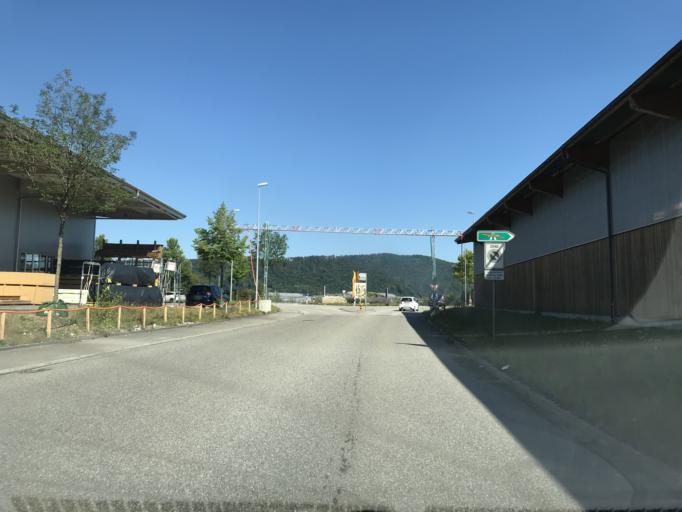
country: CH
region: Aargau
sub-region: Bezirk Rheinfelden
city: Kaiseraugst
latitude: 47.5403
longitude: 7.7457
